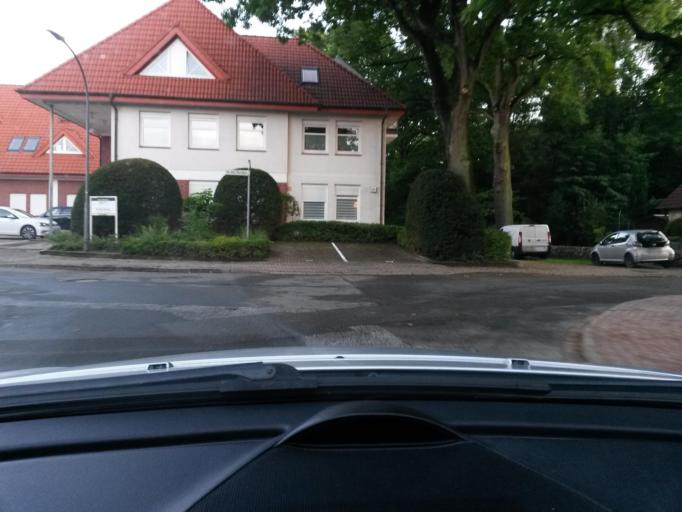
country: DE
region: Schleswig-Holstein
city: Barsbuettel
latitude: 53.5644
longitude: 10.1681
